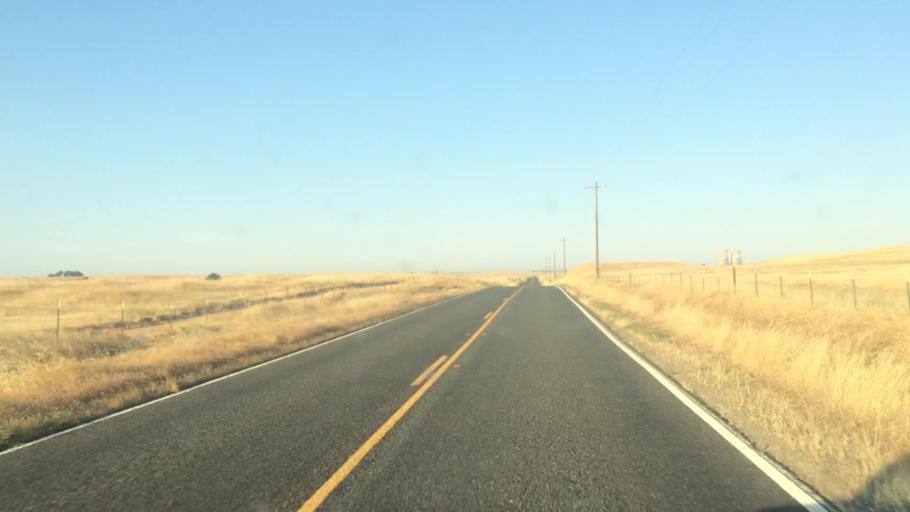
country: US
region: California
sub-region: Sacramento County
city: Clay
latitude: 38.3564
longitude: -121.0656
